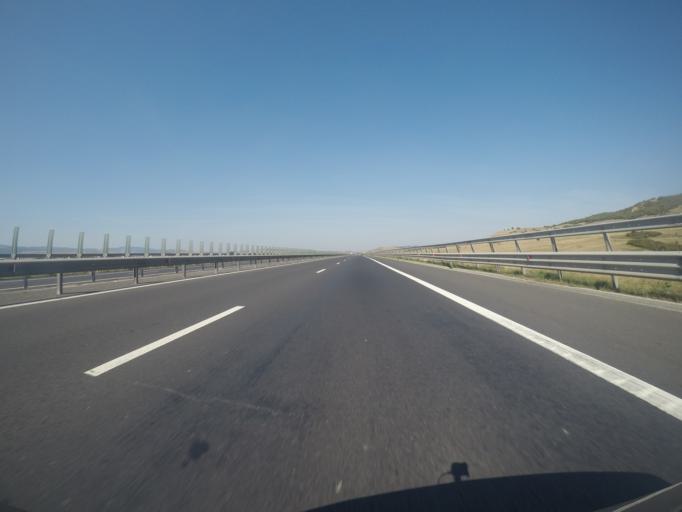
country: RO
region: Sibiu
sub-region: Oras Miercurea Sibiului
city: Miercurea Sibiului
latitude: 45.8938
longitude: 23.8209
